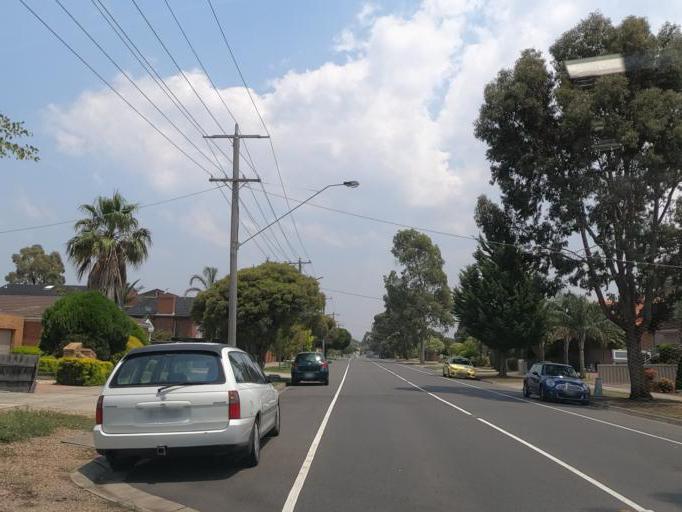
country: AU
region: Victoria
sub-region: Hume
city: Greenvale
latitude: -37.6421
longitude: 144.8923
